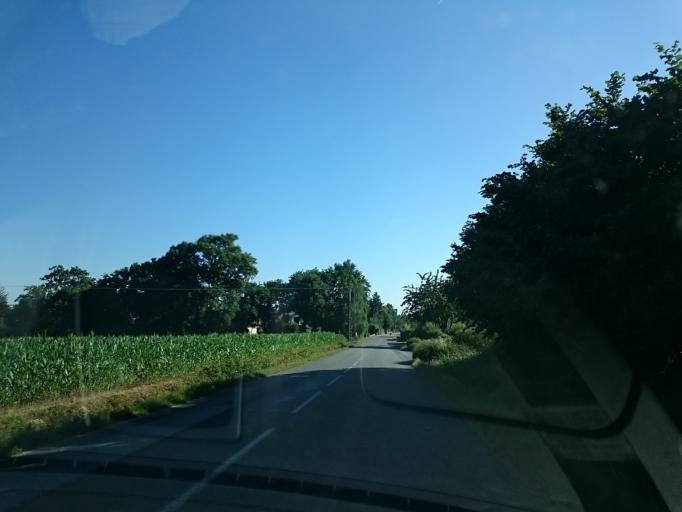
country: FR
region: Brittany
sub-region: Departement d'Ille-et-Vilaine
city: Bourgbarre
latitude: 47.9892
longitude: -1.6182
